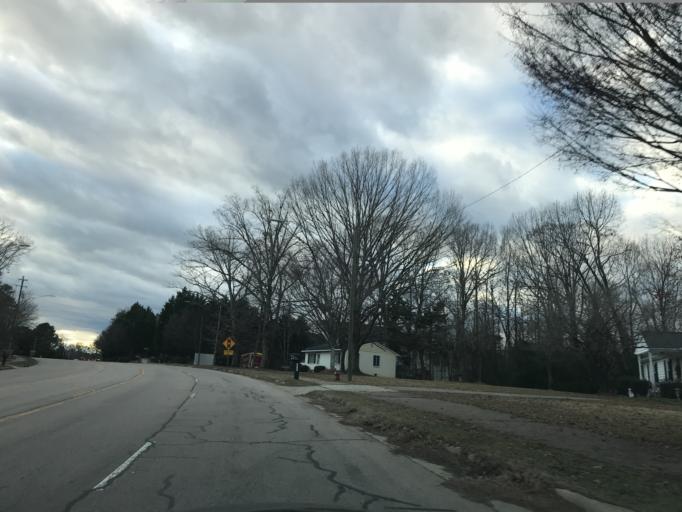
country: US
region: North Carolina
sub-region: Wake County
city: West Raleigh
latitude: 35.8723
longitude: -78.6599
